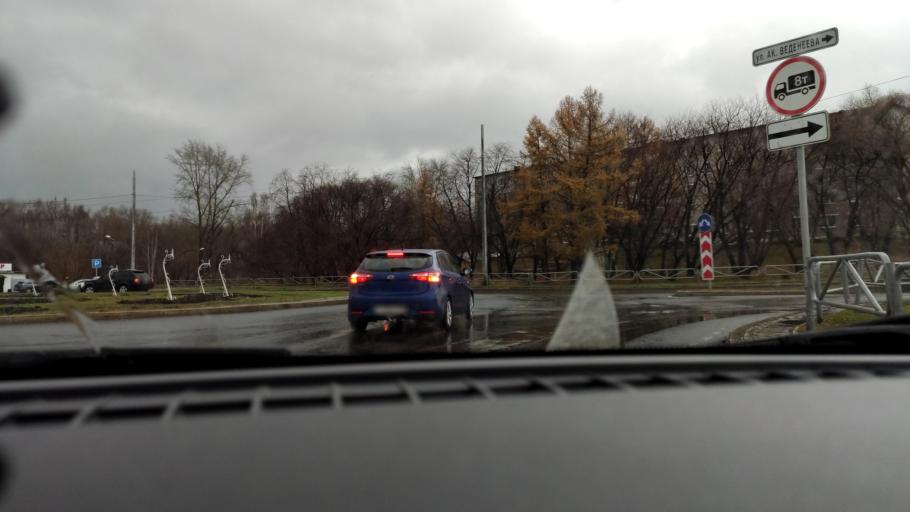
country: RU
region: Perm
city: Perm
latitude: 58.1139
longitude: 56.3668
